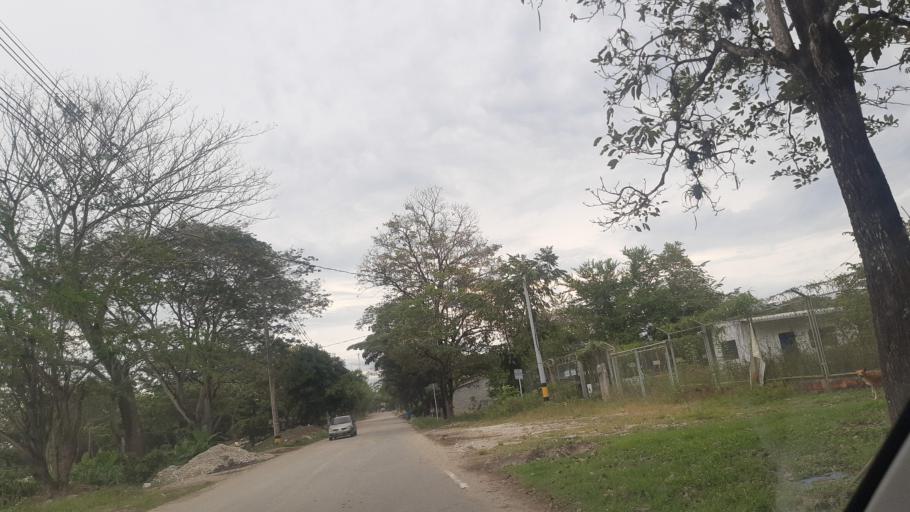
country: CO
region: Antioquia
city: Puerto Triunfo
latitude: 5.8764
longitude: -74.6364
